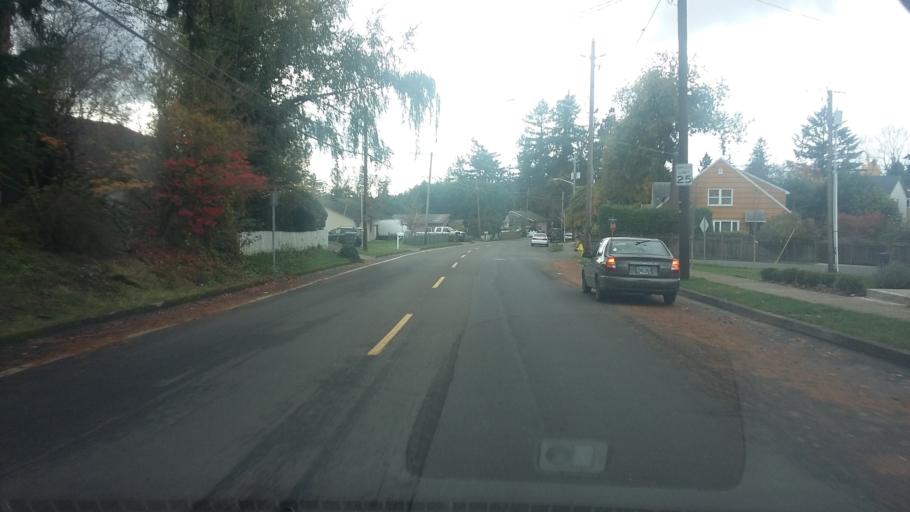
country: US
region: Washington
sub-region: Clark County
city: Camas
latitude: 45.5794
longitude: -122.4304
